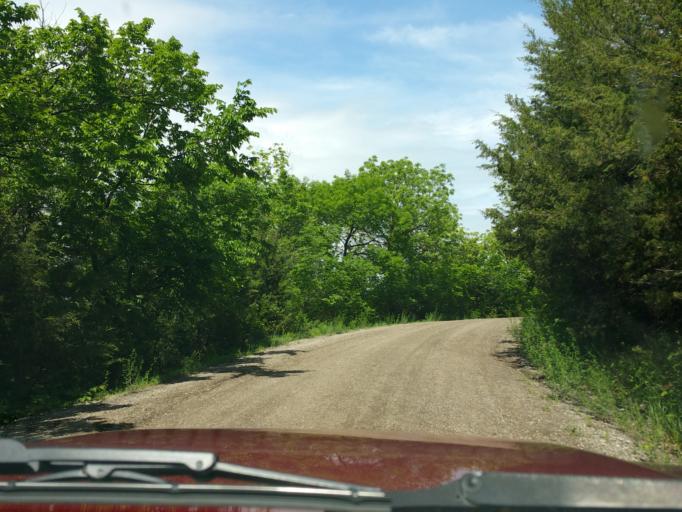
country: US
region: Kansas
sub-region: Riley County
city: Manhattan
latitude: 39.2976
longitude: -96.6517
